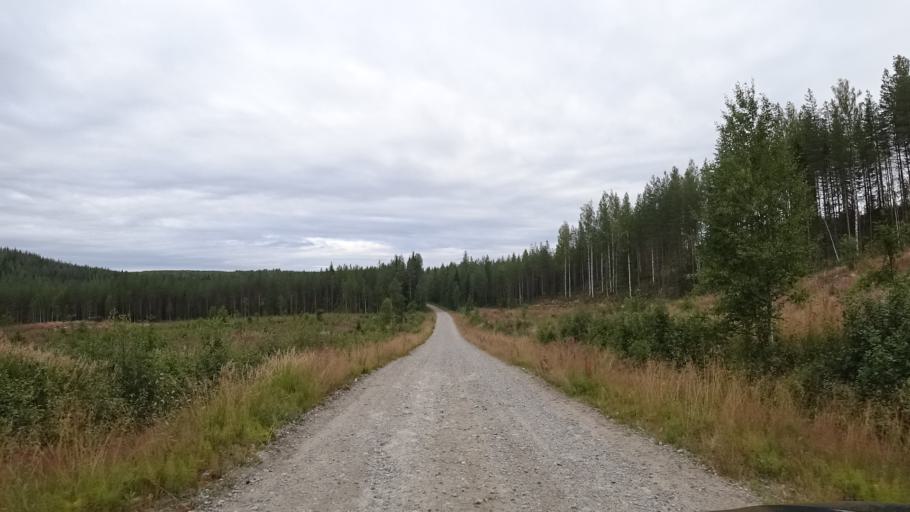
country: FI
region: North Karelia
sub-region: Joensuu
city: Ilomantsi
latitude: 63.1527
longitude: 30.6438
